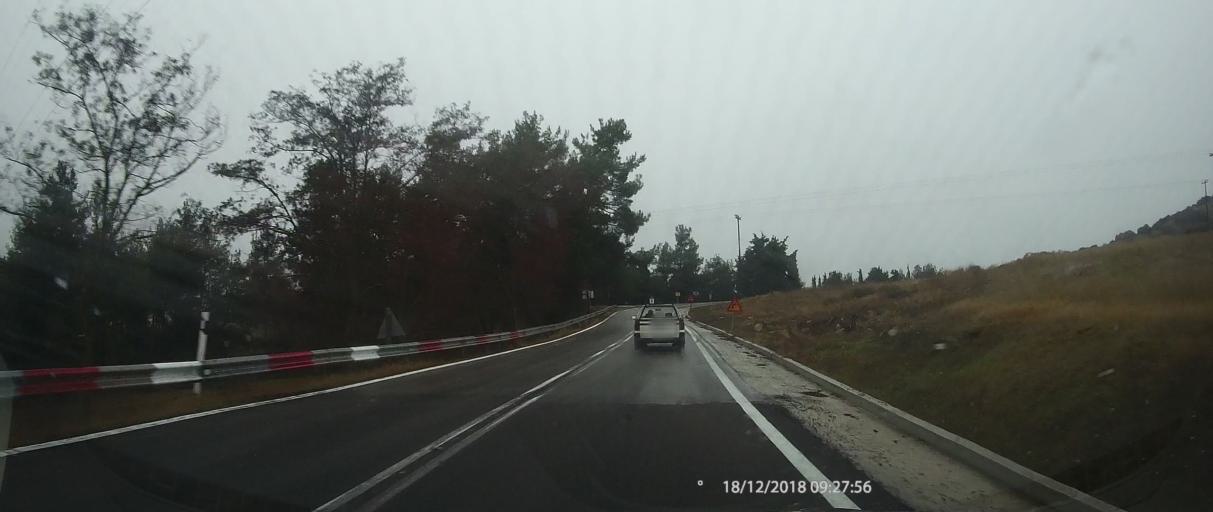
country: GR
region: Thessaly
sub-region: Nomos Larisis
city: Elassona
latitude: 39.9176
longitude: 22.1729
